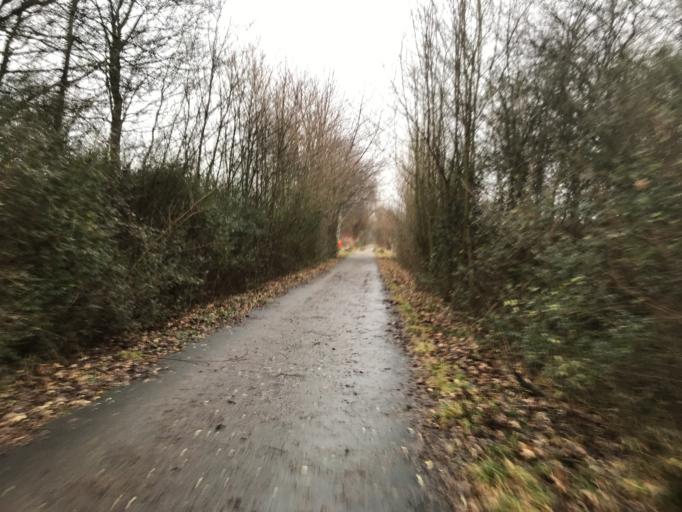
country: DE
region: Rheinland-Pfalz
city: Mommenheim
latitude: 49.8735
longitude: 8.2731
